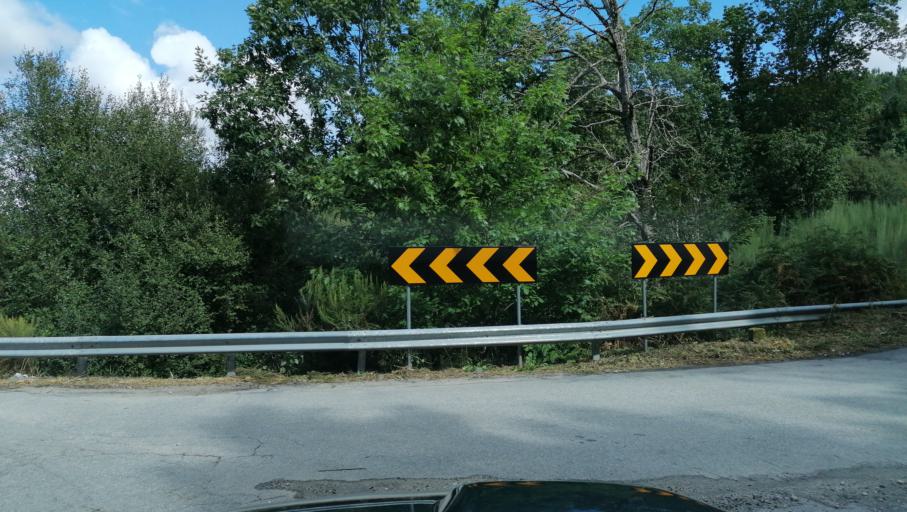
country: PT
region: Vila Real
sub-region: Vila Pouca de Aguiar
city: Vila Pouca de Aguiar
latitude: 41.5267
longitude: -7.5895
